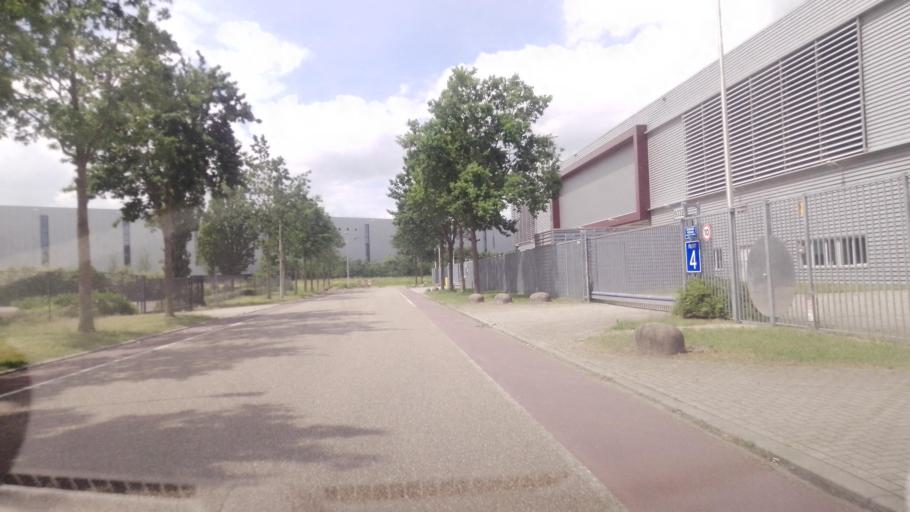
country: NL
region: Limburg
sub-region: Gemeente Peel en Maas
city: Maasbree
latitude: 51.3980
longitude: 6.0738
